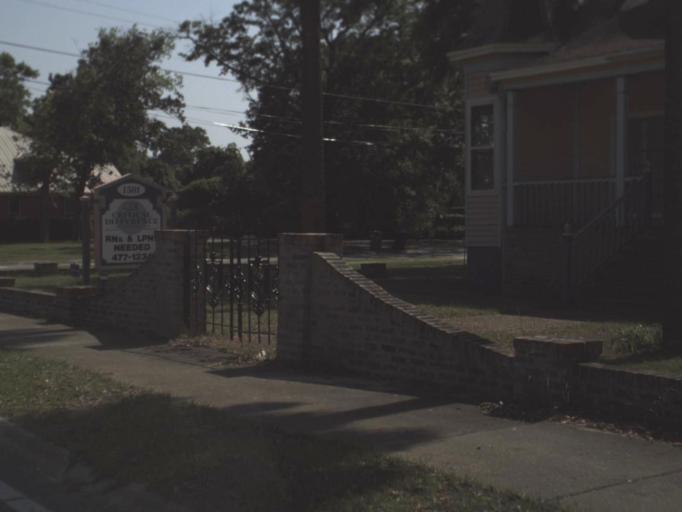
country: US
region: Florida
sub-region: Escambia County
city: Pensacola
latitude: 30.4281
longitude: -87.2083
